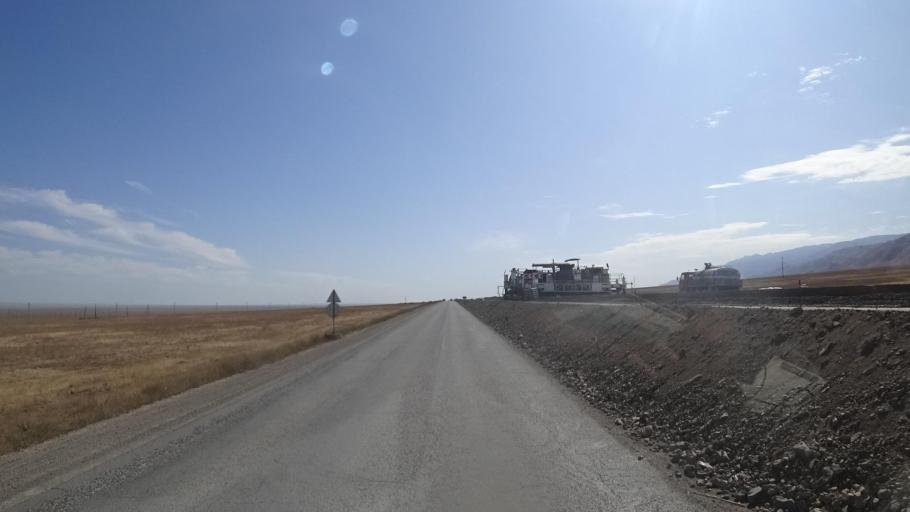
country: KG
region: Chuy
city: Ivanovka
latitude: 43.3843
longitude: 75.1742
